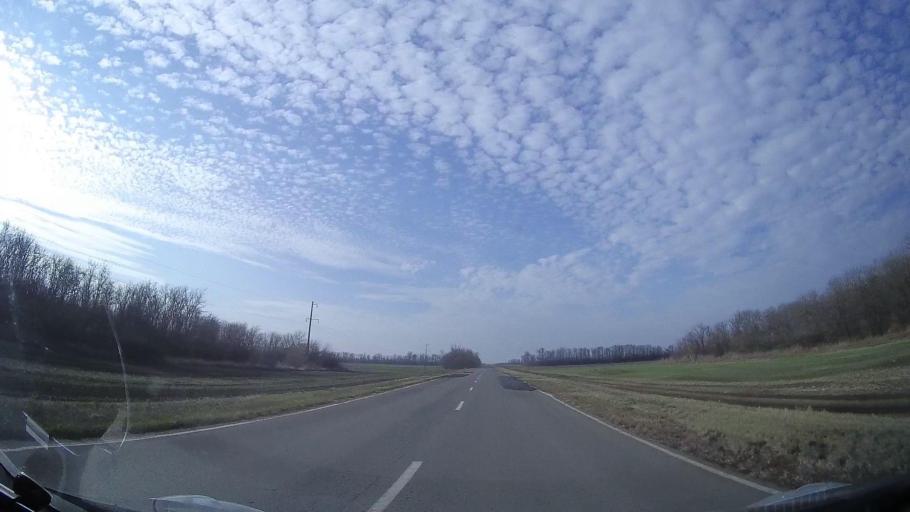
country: RU
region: Rostov
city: Veselyy
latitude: 46.9700
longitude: 40.7127
